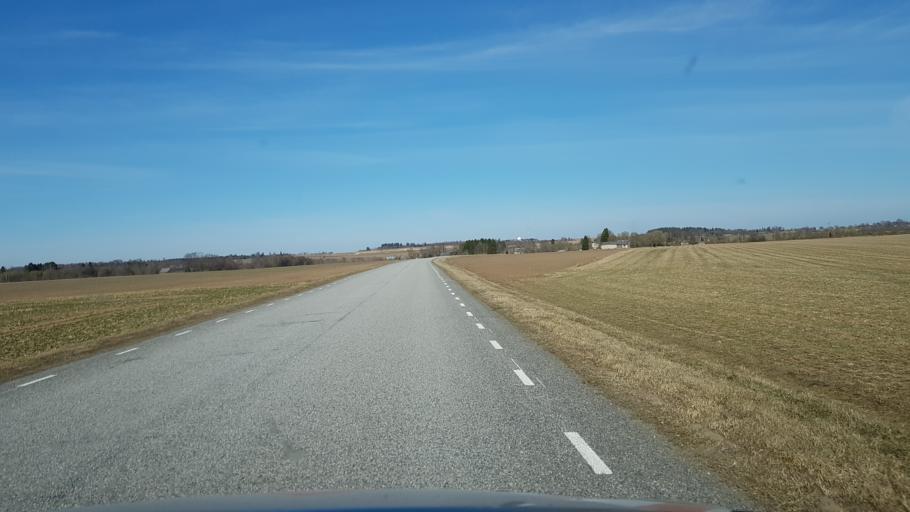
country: EE
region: Laeaene-Virumaa
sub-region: Vaeike-Maarja vald
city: Vaike-Maarja
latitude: 59.0616
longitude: 26.4713
